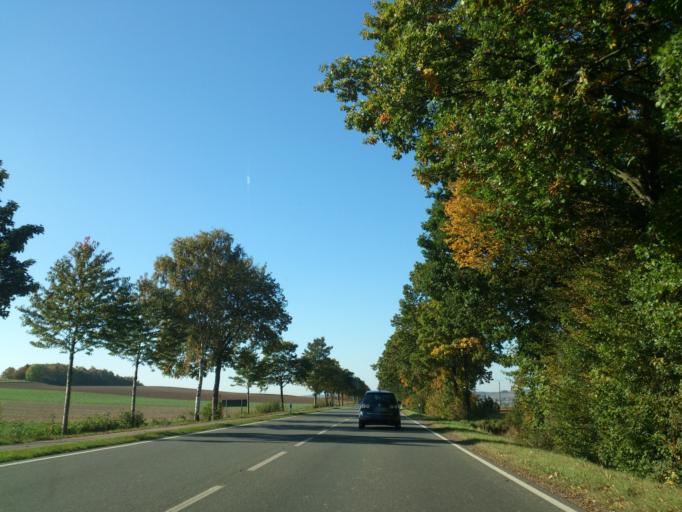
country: DE
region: North Rhine-Westphalia
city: Warburg
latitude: 51.5035
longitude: 9.1045
